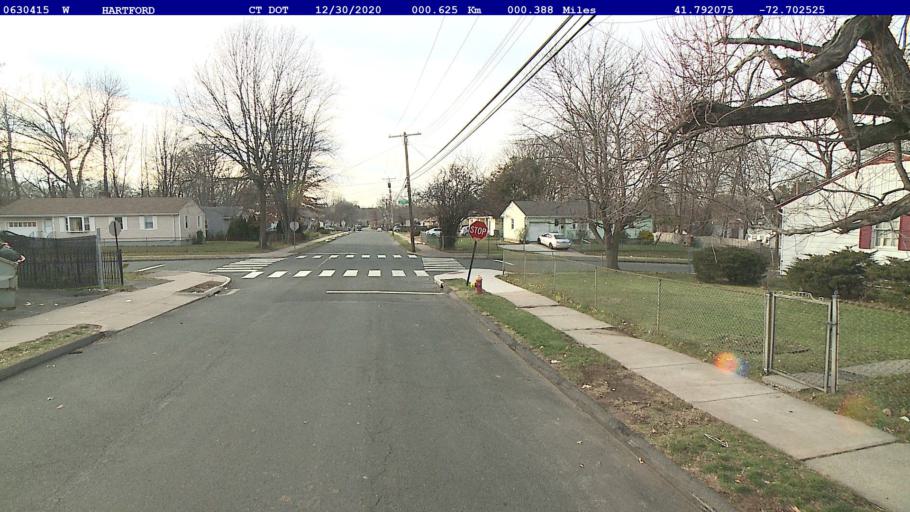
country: US
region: Connecticut
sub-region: Hartford County
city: Blue Hills
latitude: 41.7921
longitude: -72.7025
